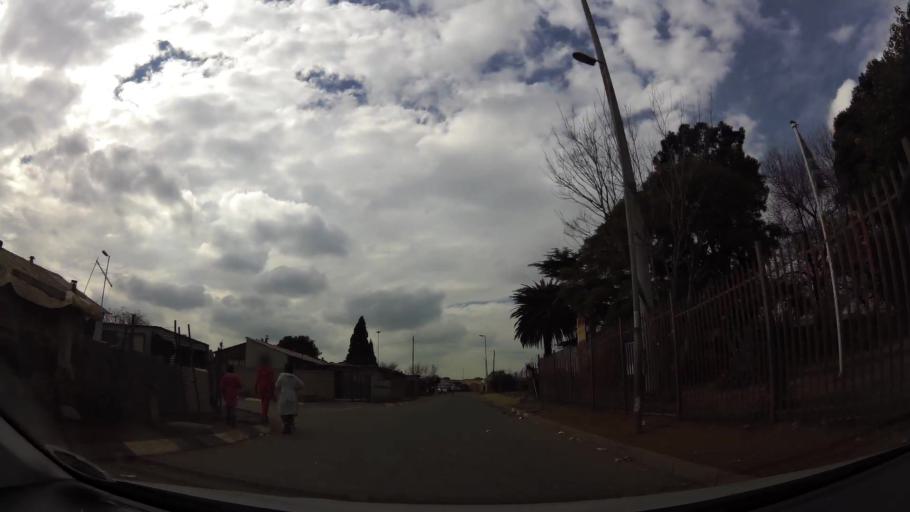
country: ZA
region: Gauteng
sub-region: City of Johannesburg Metropolitan Municipality
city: Soweto
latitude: -26.2709
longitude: 27.8512
